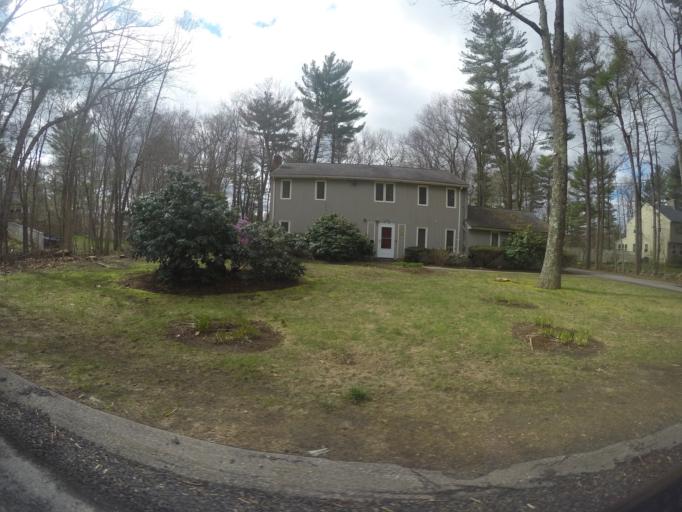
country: US
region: Massachusetts
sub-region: Bristol County
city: Easton
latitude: 42.0326
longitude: -71.1220
